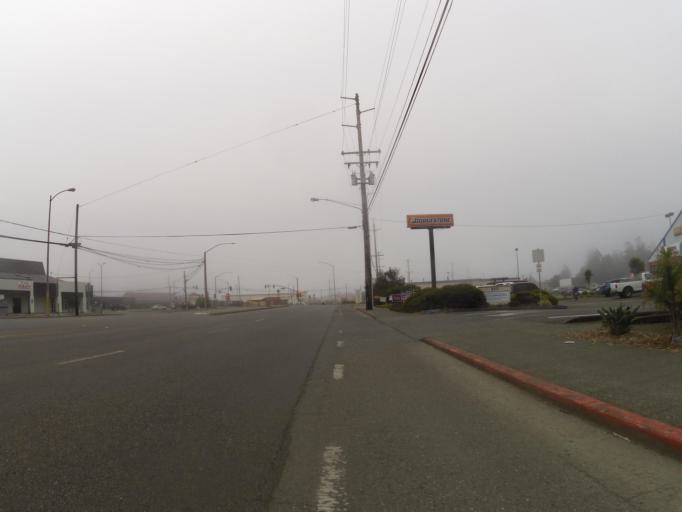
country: US
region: California
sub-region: Del Norte County
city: Crescent City
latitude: 41.7646
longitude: -124.1978
